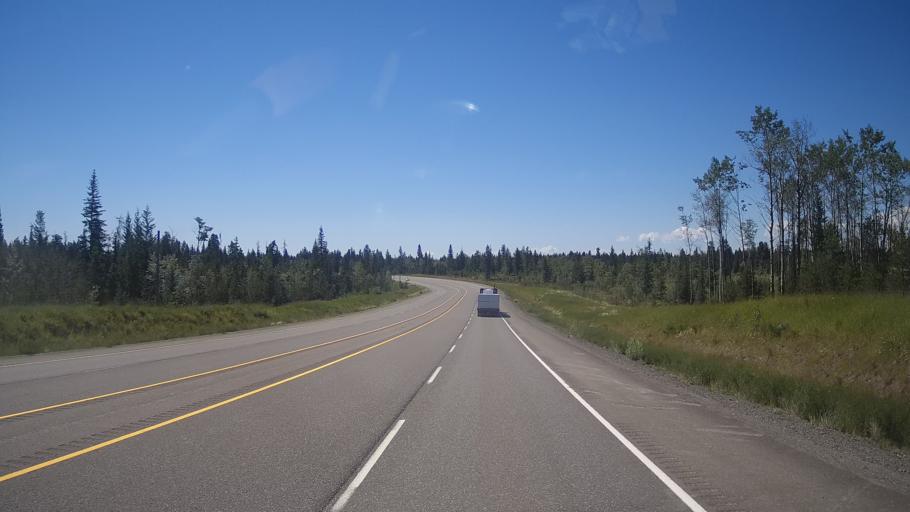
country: CA
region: British Columbia
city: Cache Creek
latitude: 51.4253
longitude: -121.3785
